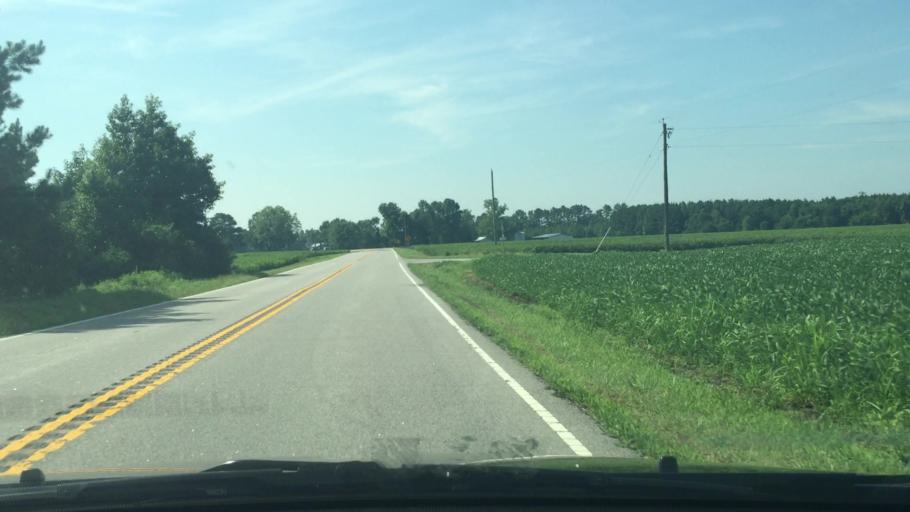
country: US
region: Virginia
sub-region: Southampton County
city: Courtland
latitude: 36.8463
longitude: -77.1326
